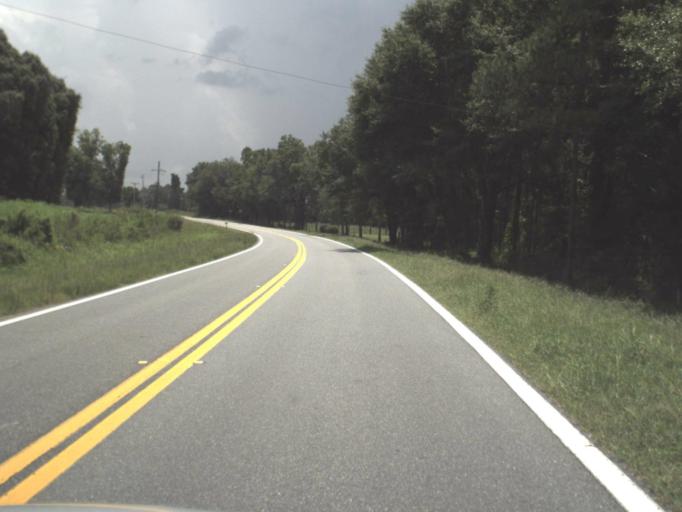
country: US
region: Florida
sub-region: Union County
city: Lake Butler
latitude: 29.8915
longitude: -82.3485
